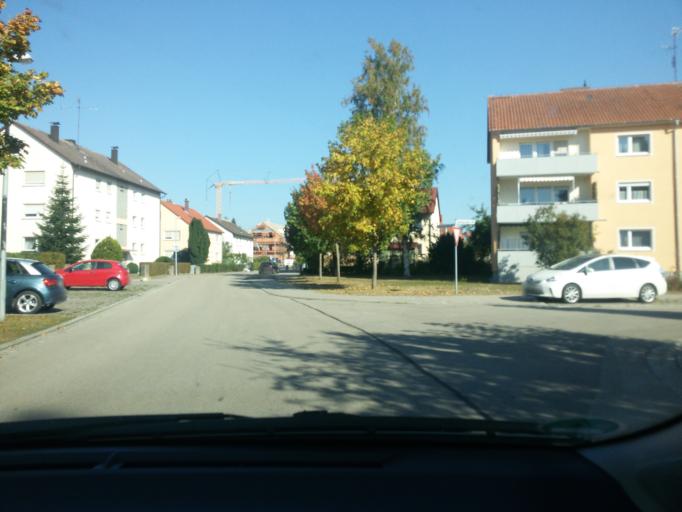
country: DE
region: Bavaria
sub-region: Regierungsbezirk Mittelfranken
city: Wassertrudingen
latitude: 49.0429
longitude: 10.5949
